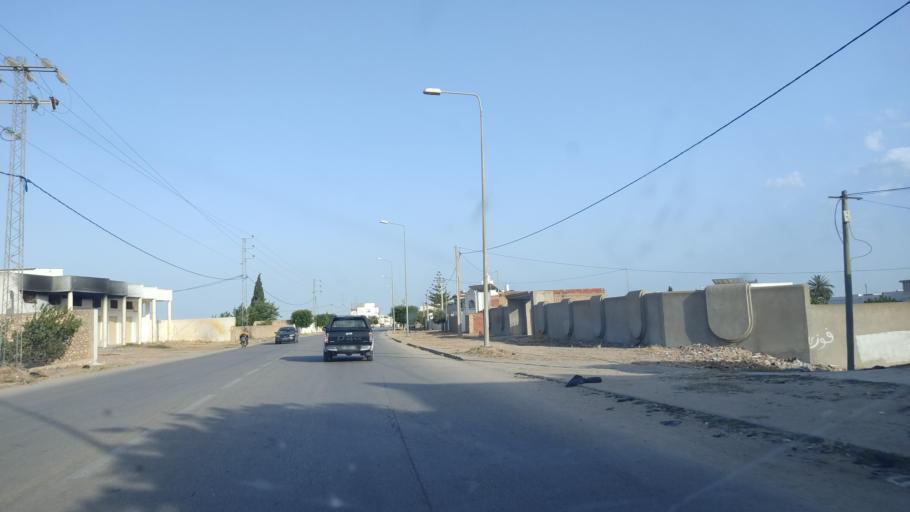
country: TN
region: Safaqis
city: Sfax
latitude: 34.7930
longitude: 10.6847
